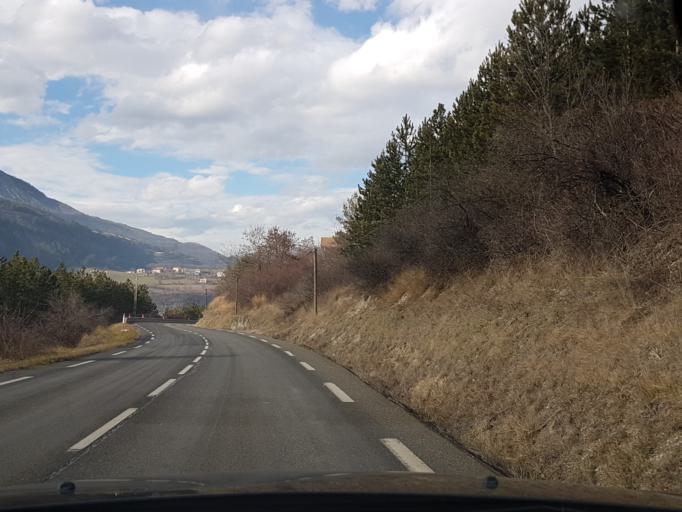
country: FR
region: Provence-Alpes-Cote d'Azur
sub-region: Departement des Hautes-Alpes
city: Tallard
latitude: 44.4679
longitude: 6.1390
